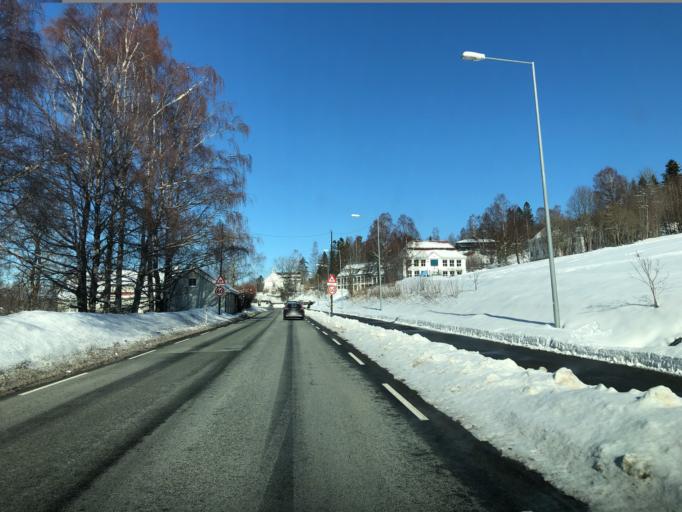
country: NO
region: Buskerud
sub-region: Lier
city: Tranby
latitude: 59.8267
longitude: 10.2559
